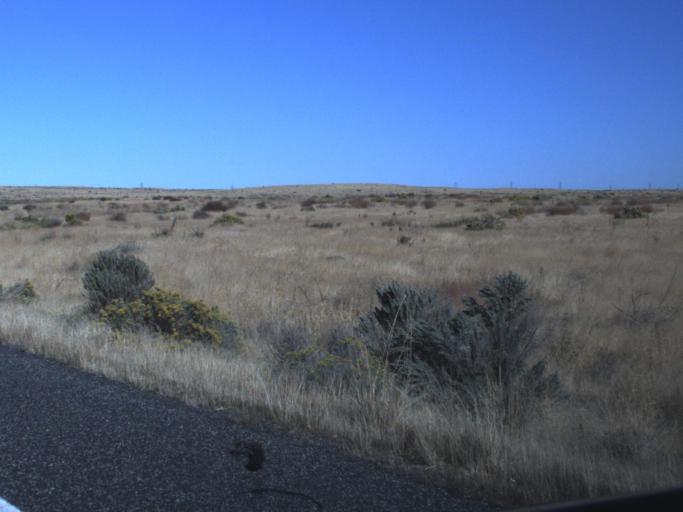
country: US
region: Washington
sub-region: Benton County
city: West Richland
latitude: 46.3780
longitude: -119.4131
